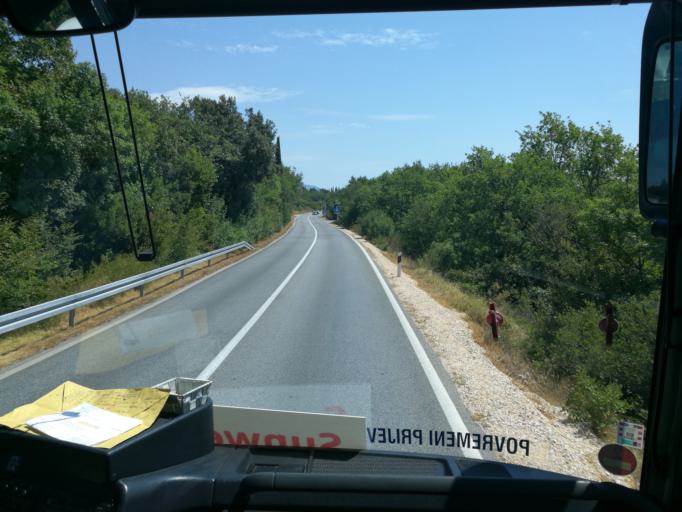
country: HR
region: Dubrovacko-Neretvanska
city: Cavtat
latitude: 42.5645
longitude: 18.2472
